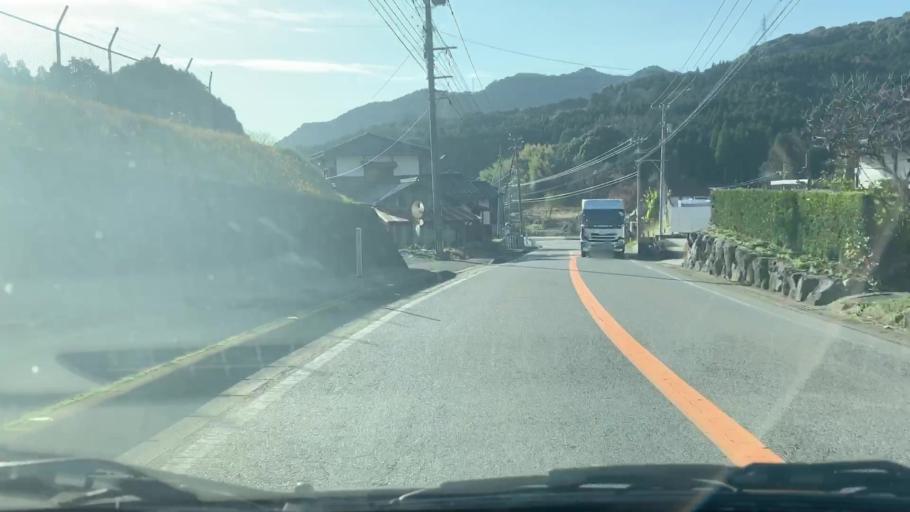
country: JP
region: Saga Prefecture
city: Takeocho-takeo
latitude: 33.2350
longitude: 130.0127
